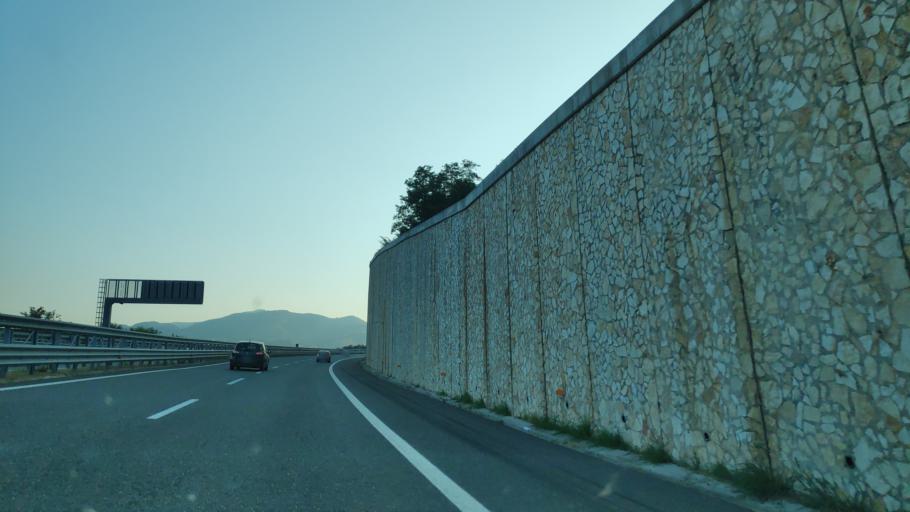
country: IT
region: Calabria
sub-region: Provincia di Catanzaro
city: Nocera Scalo
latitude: 39.0375
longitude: 16.1370
